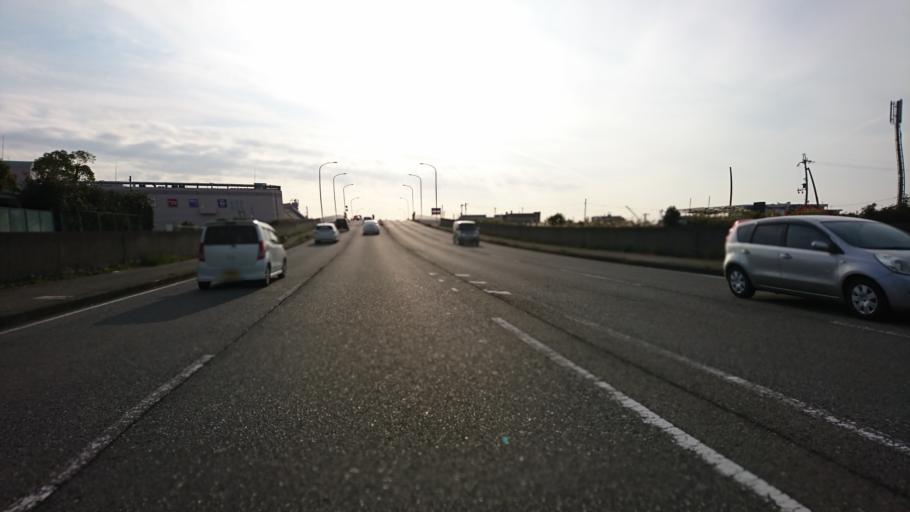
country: JP
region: Hyogo
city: Kakogawacho-honmachi
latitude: 34.7075
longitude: 134.8793
